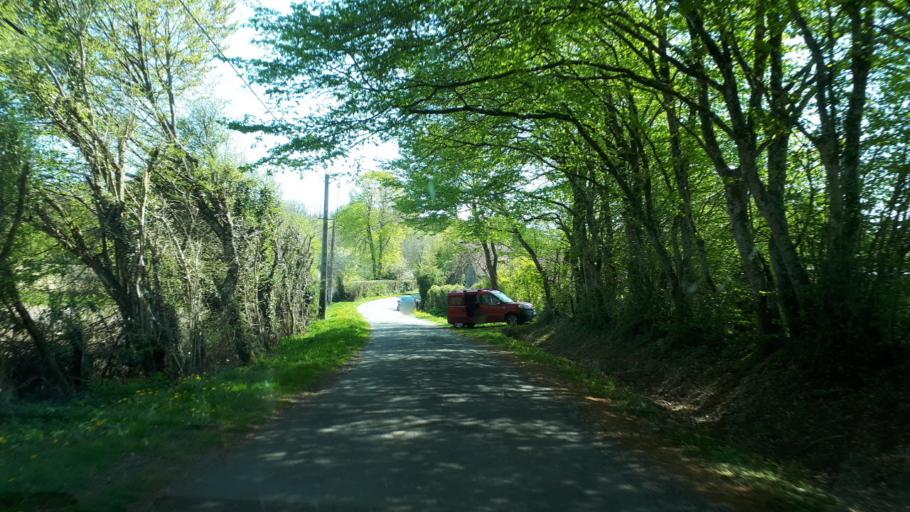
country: FR
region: Centre
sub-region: Departement du Cher
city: Henrichemont
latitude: 47.2990
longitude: 2.5766
